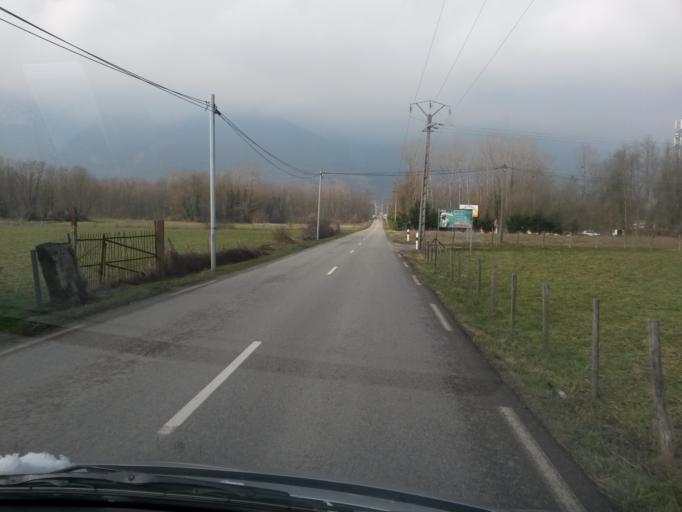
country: FR
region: Rhone-Alpes
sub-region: Departement de l'Isere
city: Tencin
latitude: 45.3130
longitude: 5.9497
